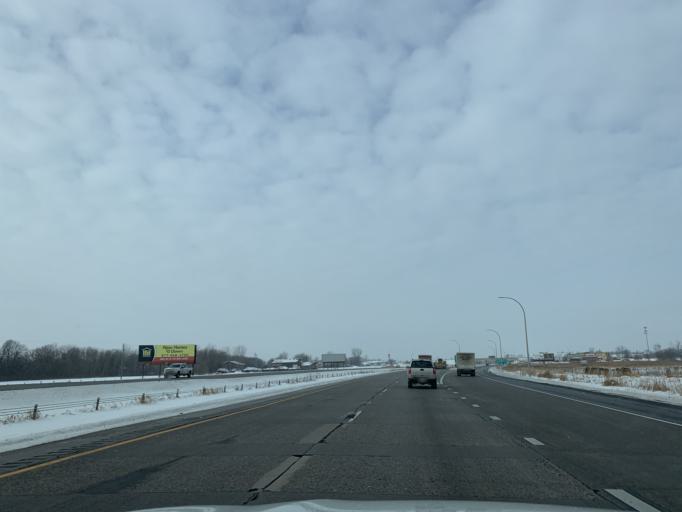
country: US
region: Minnesota
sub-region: Wright County
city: Albertville
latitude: 45.2332
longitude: -93.6412
